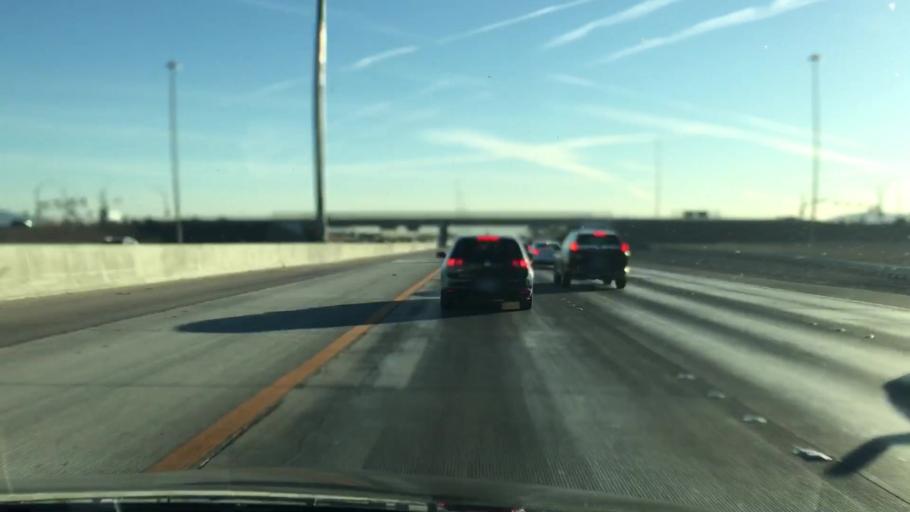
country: US
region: Nevada
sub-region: Clark County
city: Enterprise
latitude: 36.0664
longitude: -115.2453
